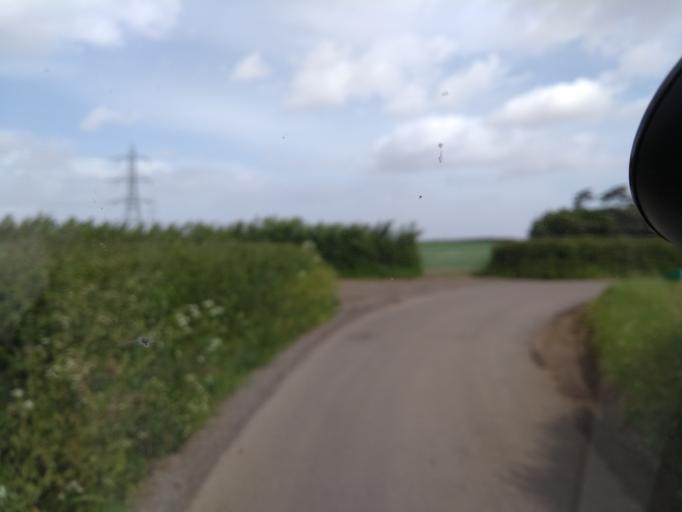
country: GB
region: England
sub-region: Somerset
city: Bridgwater
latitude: 51.1812
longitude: -3.0944
